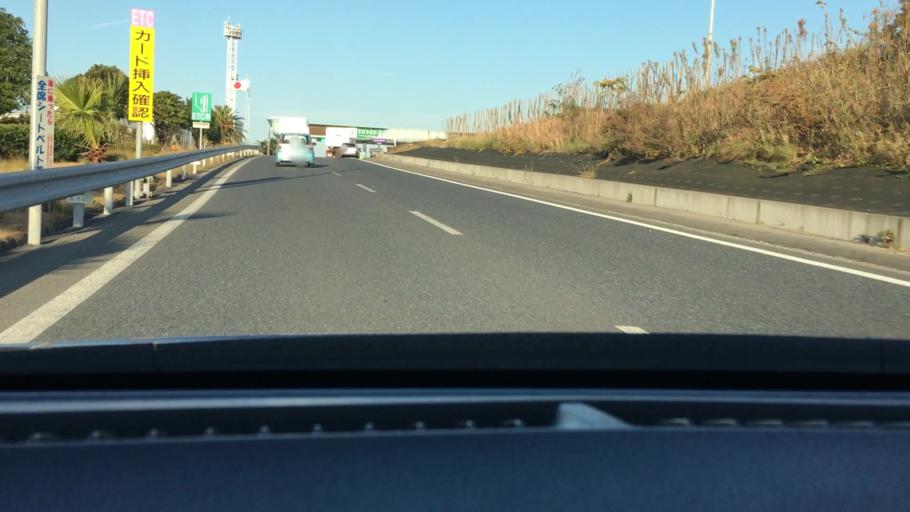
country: JP
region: Chiba
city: Kisarazu
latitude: 35.4344
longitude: 139.9203
